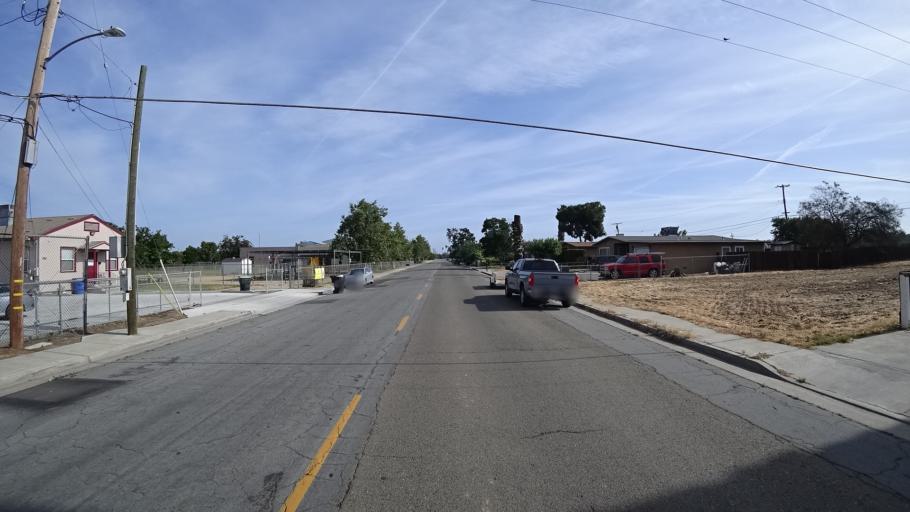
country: US
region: California
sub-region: Kings County
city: Home Garden
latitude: 36.3146
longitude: -119.6426
